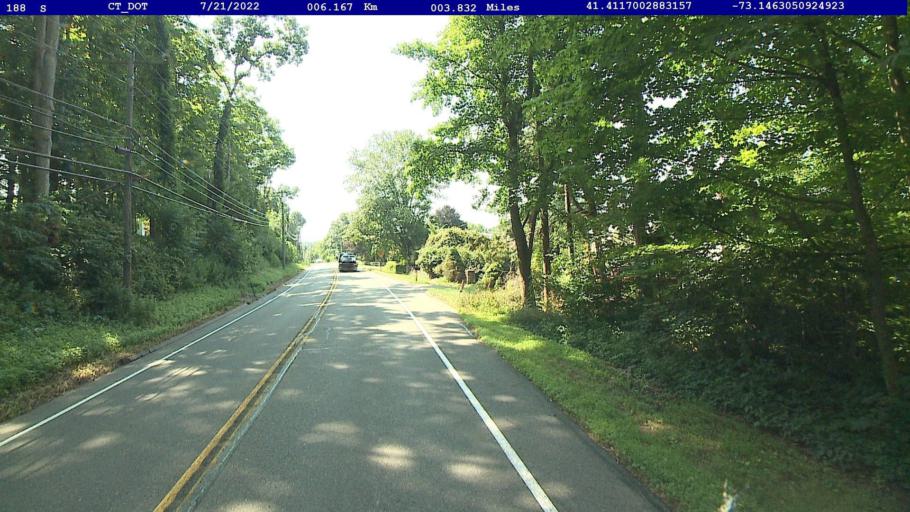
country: US
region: Connecticut
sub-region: New Haven County
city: Oxford
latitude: 41.4117
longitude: -73.1463
